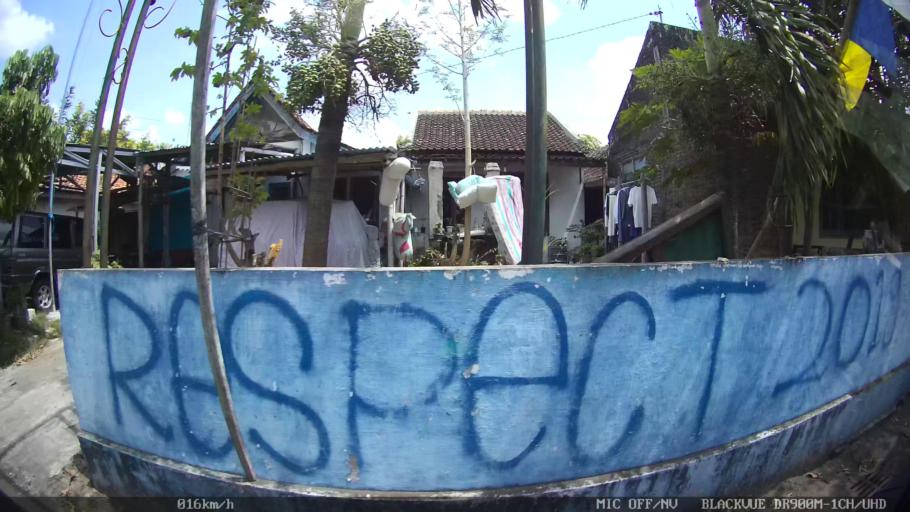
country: ID
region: Daerah Istimewa Yogyakarta
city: Gamping Lor
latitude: -7.8055
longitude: 110.3462
